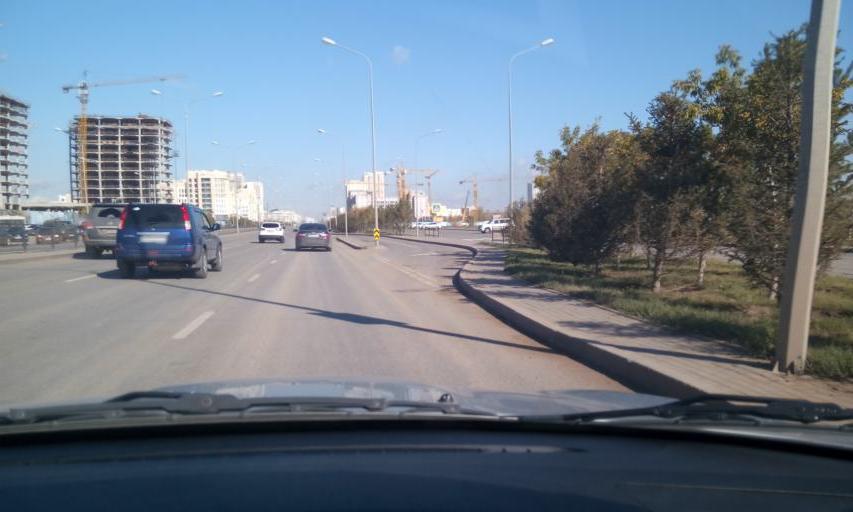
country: KZ
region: Astana Qalasy
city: Astana
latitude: 51.0876
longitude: 71.4242
